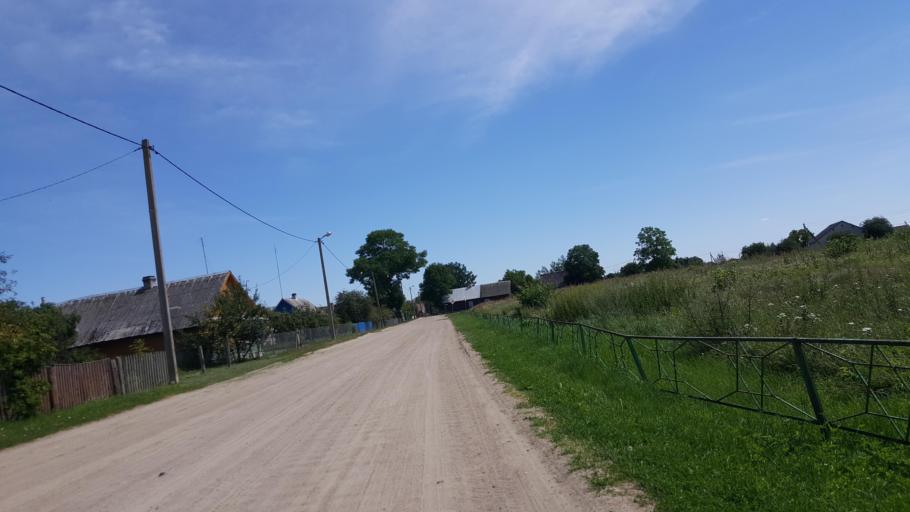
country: BY
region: Brest
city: Pruzhany
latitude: 52.5563
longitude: 24.2053
